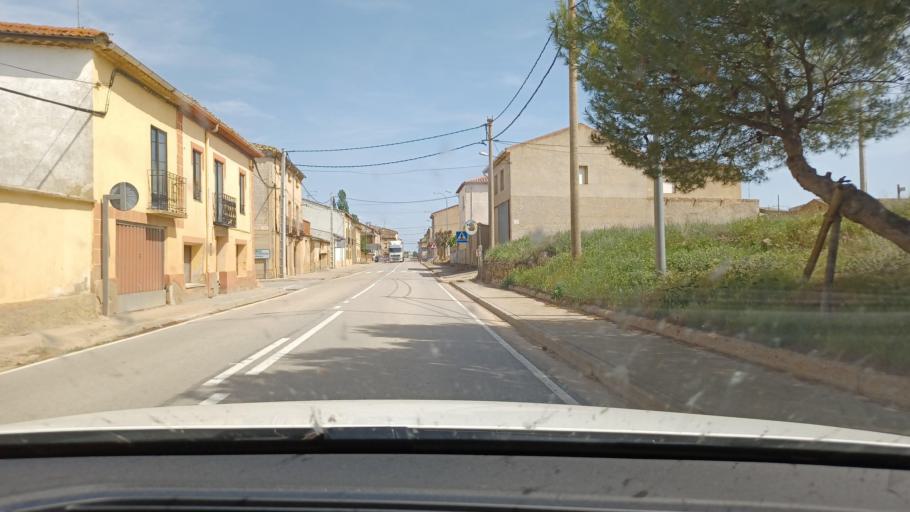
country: ES
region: Castille and Leon
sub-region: Provincia de Soria
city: Monteagudo de las Vicarias
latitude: 41.3664
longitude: -2.1715
